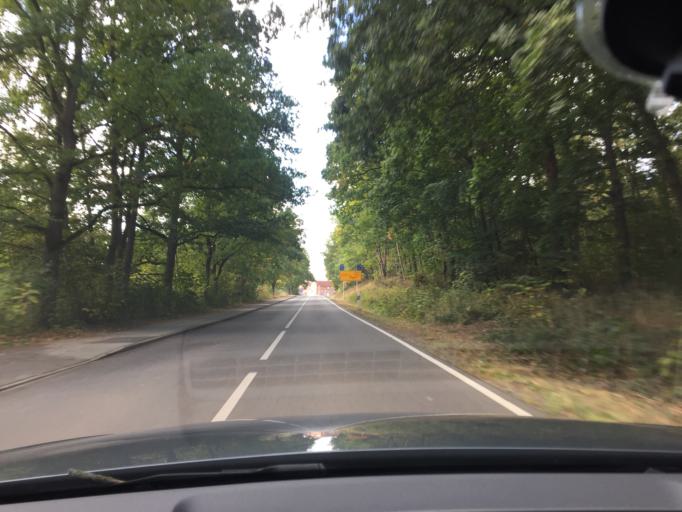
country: DE
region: Mecklenburg-Vorpommern
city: Krakow am See
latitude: 53.6698
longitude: 12.2713
